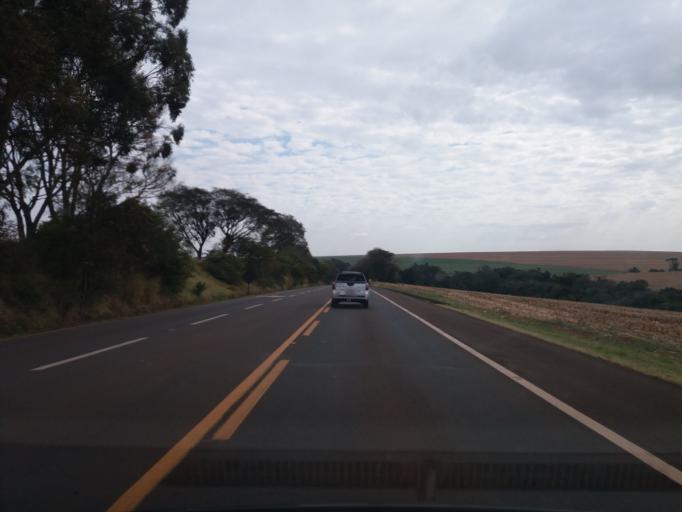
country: BR
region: Parana
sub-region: Campo Mourao
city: Campo Mourao
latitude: -24.3196
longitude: -52.6333
